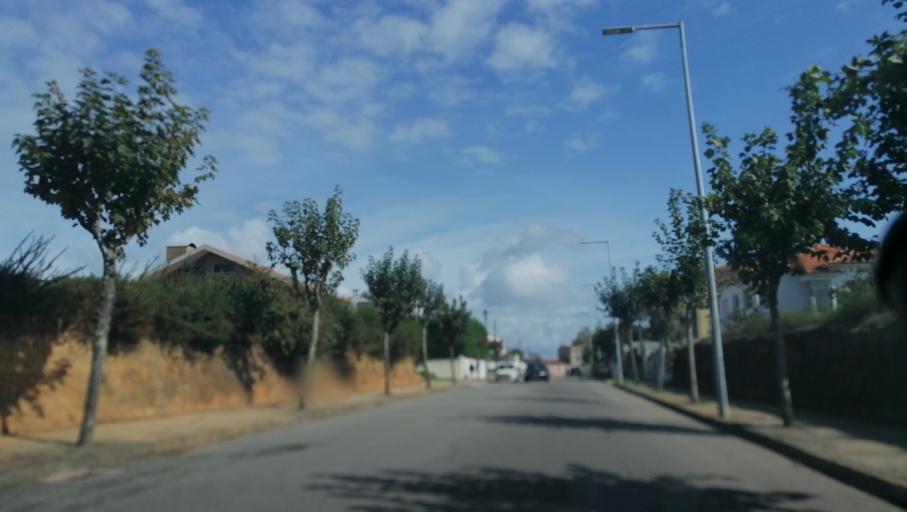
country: PT
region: Aveiro
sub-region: Espinho
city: Silvalde
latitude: 41.0040
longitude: -8.6254
